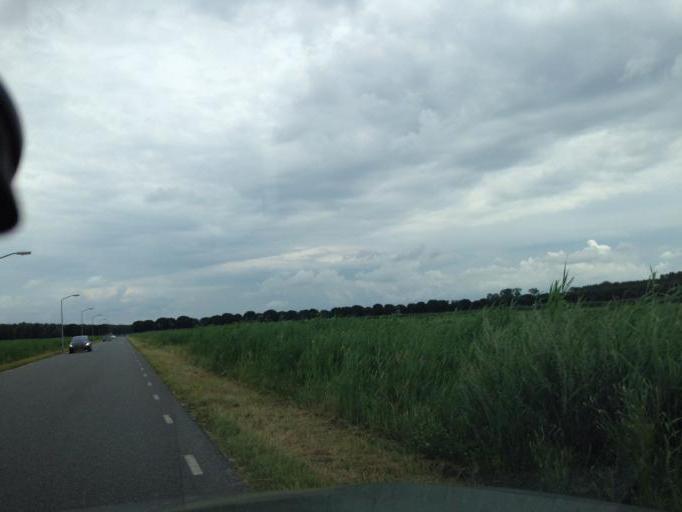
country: NL
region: Flevoland
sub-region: Gemeente Almere
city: Almere Stad
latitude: 52.3601
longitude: 5.2886
